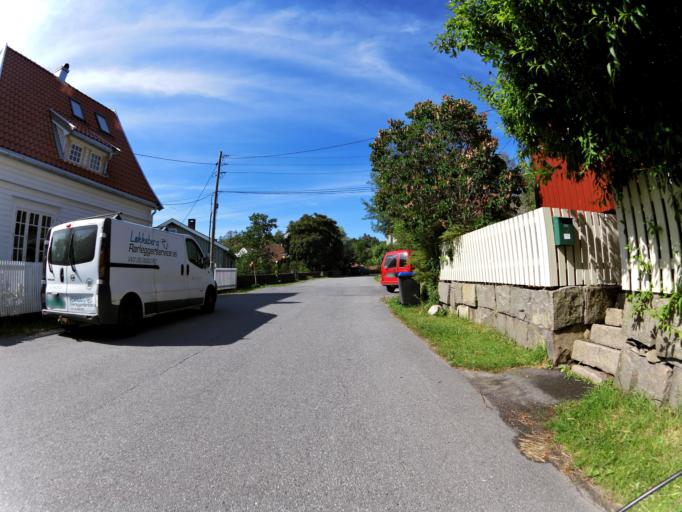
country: NO
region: Ostfold
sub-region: Fredrikstad
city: Fredrikstad
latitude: 59.2211
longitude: 10.9386
